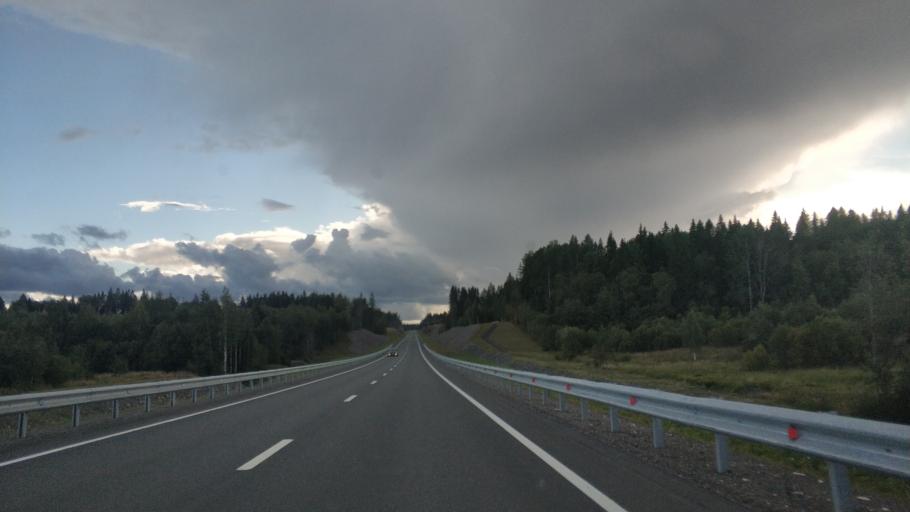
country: RU
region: Republic of Karelia
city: Lakhdenpokh'ya
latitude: 61.4434
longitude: 29.9877
